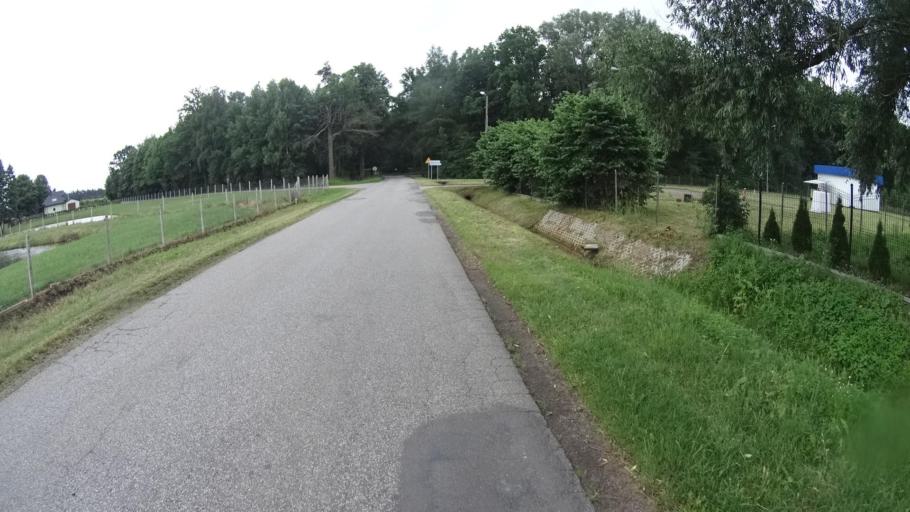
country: PL
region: Masovian Voivodeship
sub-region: Powiat grojecki
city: Goszczyn
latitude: 51.7828
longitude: 20.8543
